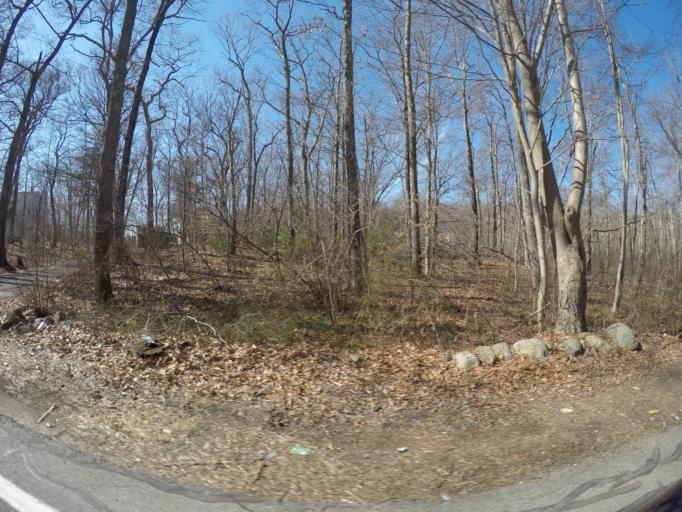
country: US
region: Massachusetts
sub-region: Bristol County
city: Easton
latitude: 42.0807
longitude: -71.1396
